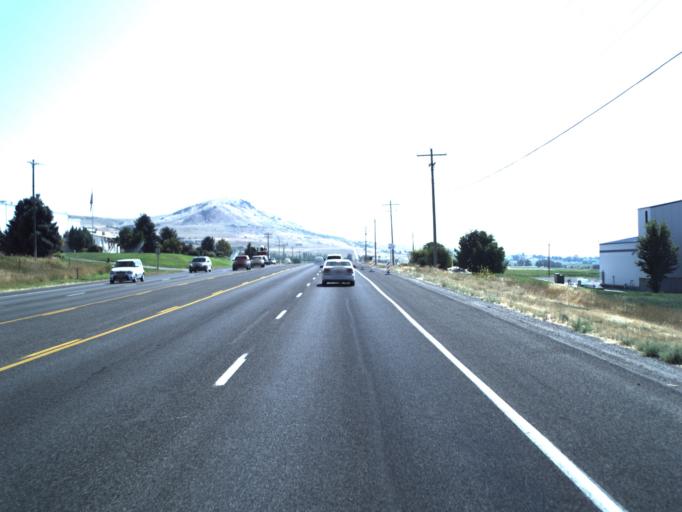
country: US
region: Utah
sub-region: Cache County
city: Richmond
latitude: 41.9095
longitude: -111.8147
